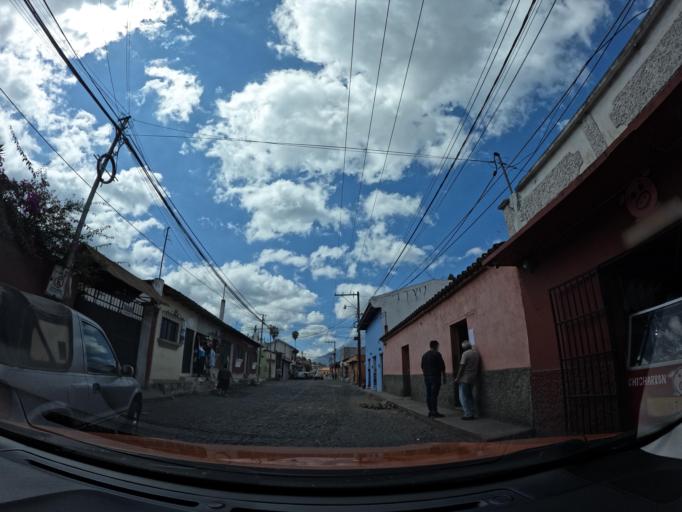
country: GT
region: Sacatepequez
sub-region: Municipio de Santa Maria de Jesus
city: Santa Maria de Jesus
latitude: 14.5317
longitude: -90.7383
